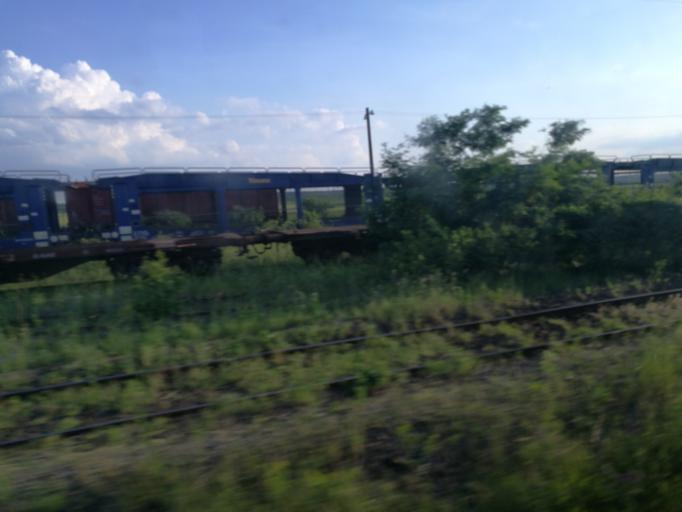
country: RO
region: Arges
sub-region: Oras Stefanesti
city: Golesti
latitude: 44.8322
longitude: 24.9866
